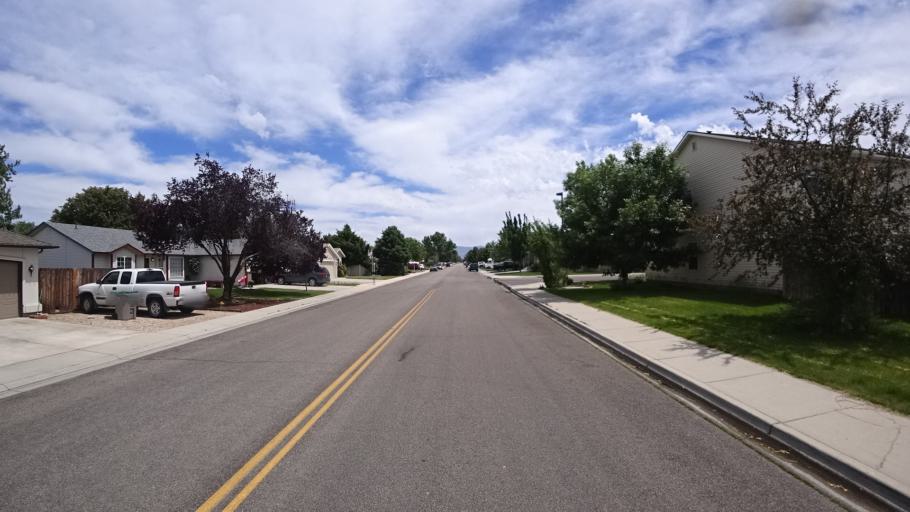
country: US
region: Idaho
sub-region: Ada County
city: Garden City
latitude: 43.6158
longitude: -116.3087
